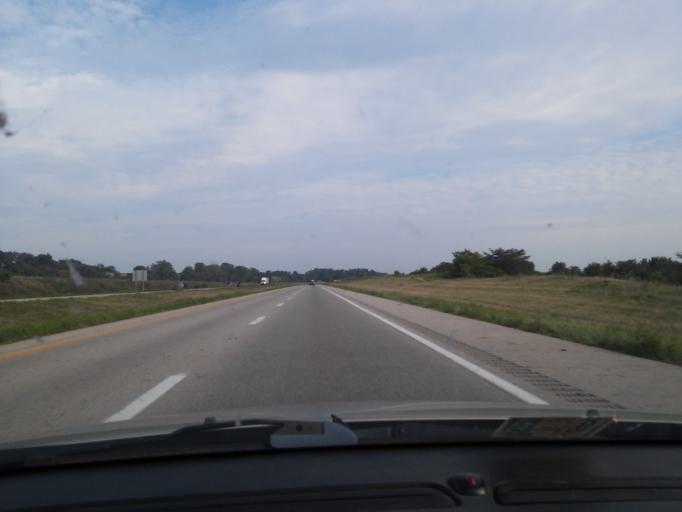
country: US
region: Ohio
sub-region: Ross County
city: Chillicothe
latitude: 39.2891
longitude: -82.8948
